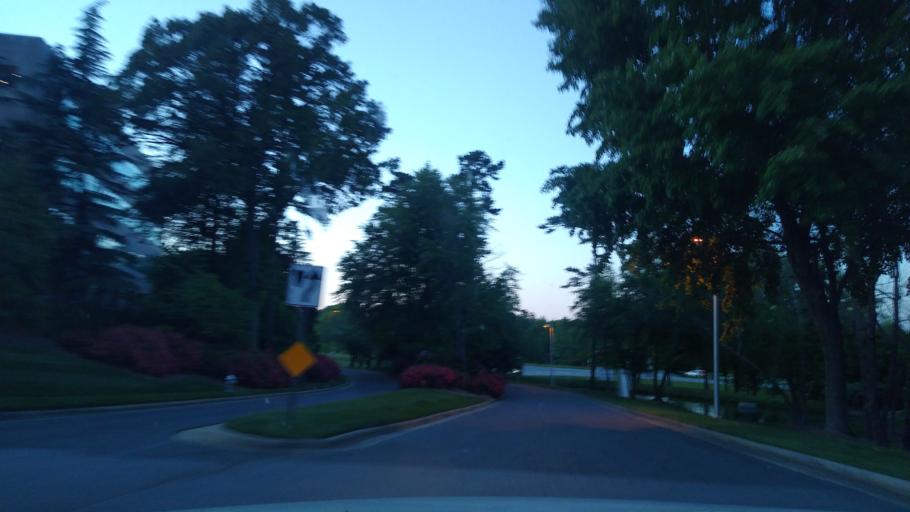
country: US
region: North Carolina
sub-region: Guilford County
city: Oak Ridge
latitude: 36.0845
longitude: -79.9632
